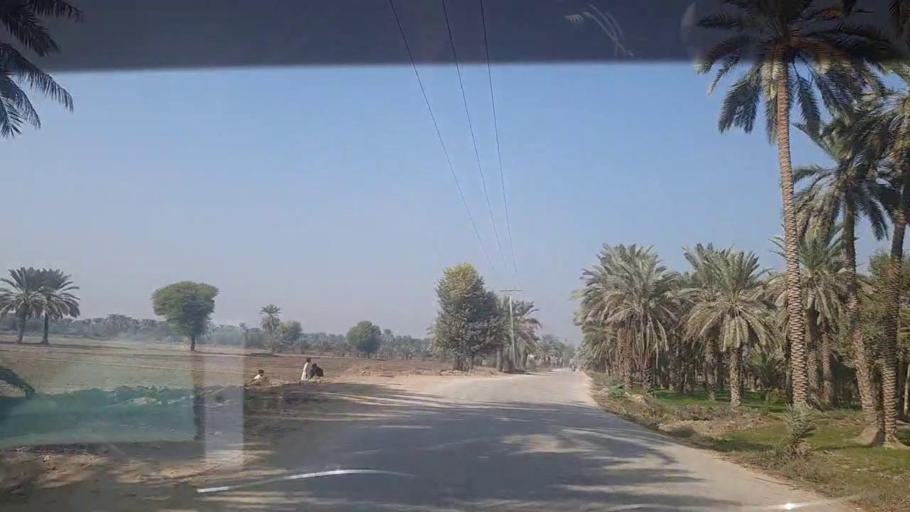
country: PK
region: Sindh
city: Kot Diji
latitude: 27.3809
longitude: 68.6897
